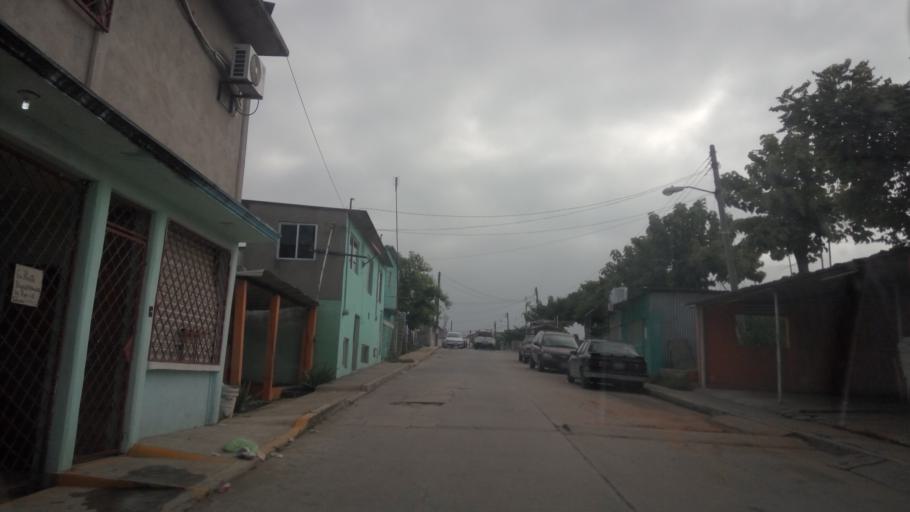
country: MX
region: Chiapas
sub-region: Reforma
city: El Carmen (El Limon)
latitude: 17.8587
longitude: -93.1523
